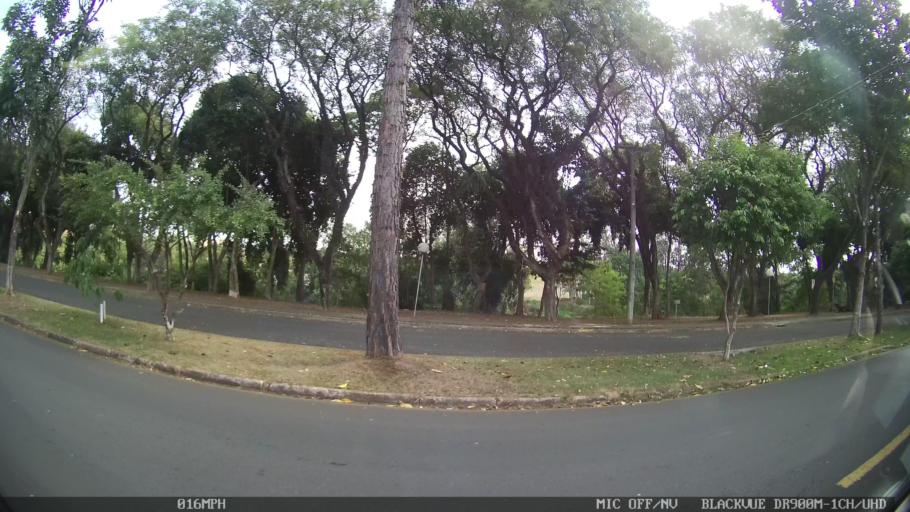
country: BR
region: Sao Paulo
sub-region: Piracicaba
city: Piracicaba
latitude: -22.7088
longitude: -47.6758
